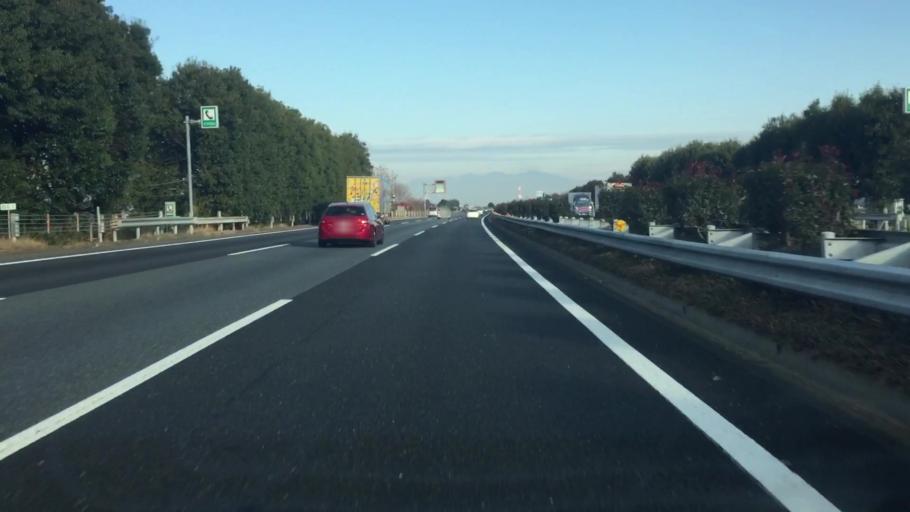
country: JP
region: Saitama
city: Honjo
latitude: 36.1814
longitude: 139.1908
